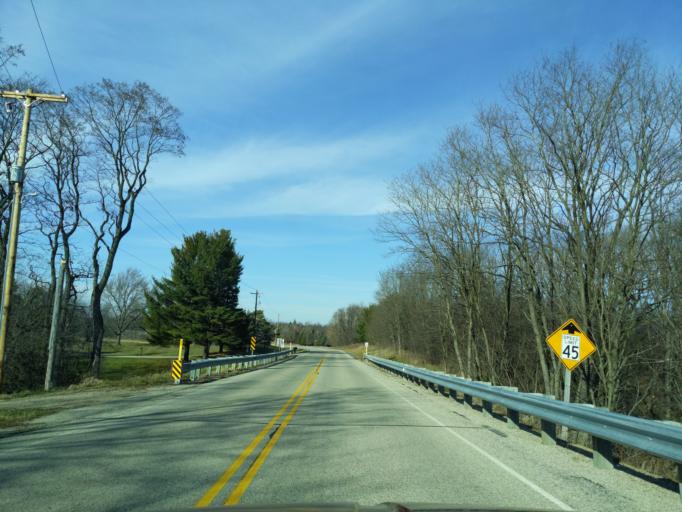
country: US
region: Wisconsin
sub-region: Walworth County
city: Elkhorn
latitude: 42.7494
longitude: -88.5930
